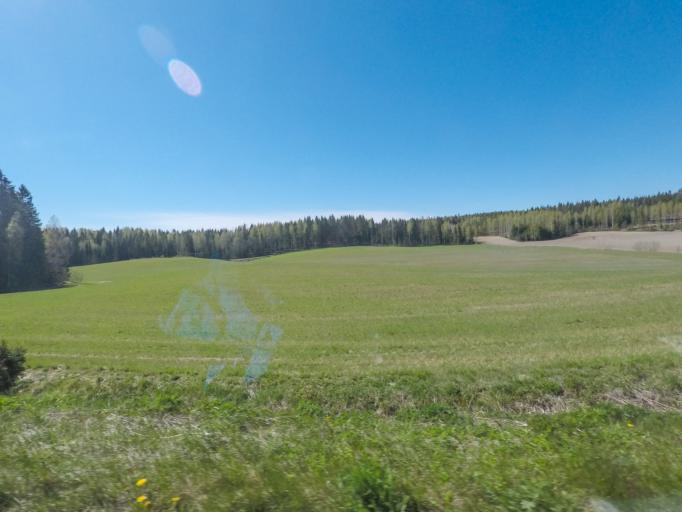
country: FI
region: Uusimaa
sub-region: Helsinki
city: Sammatti
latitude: 60.4036
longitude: 23.8182
